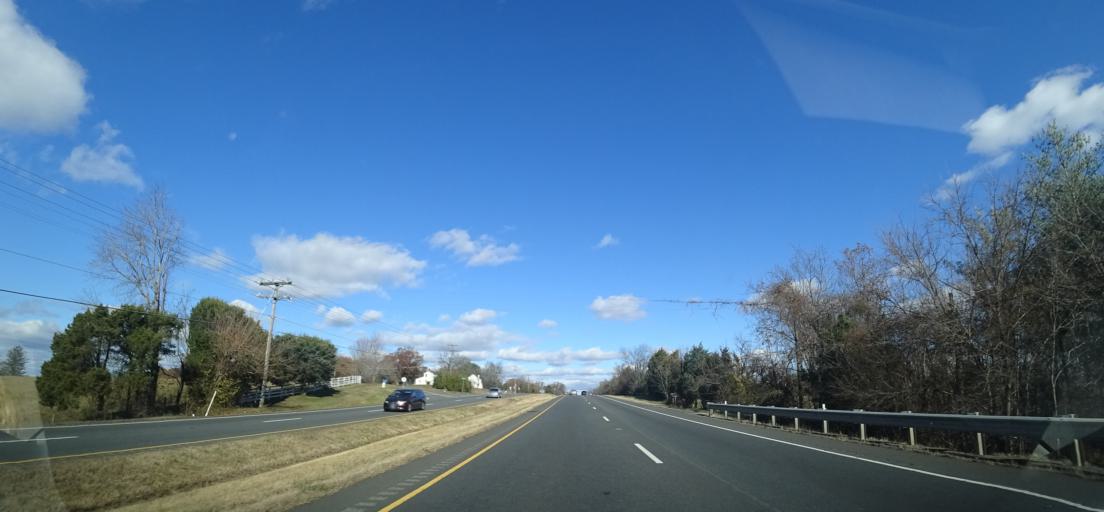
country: US
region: Virginia
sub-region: Fauquier County
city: Warrenton
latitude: 38.6515
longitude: -77.8020
